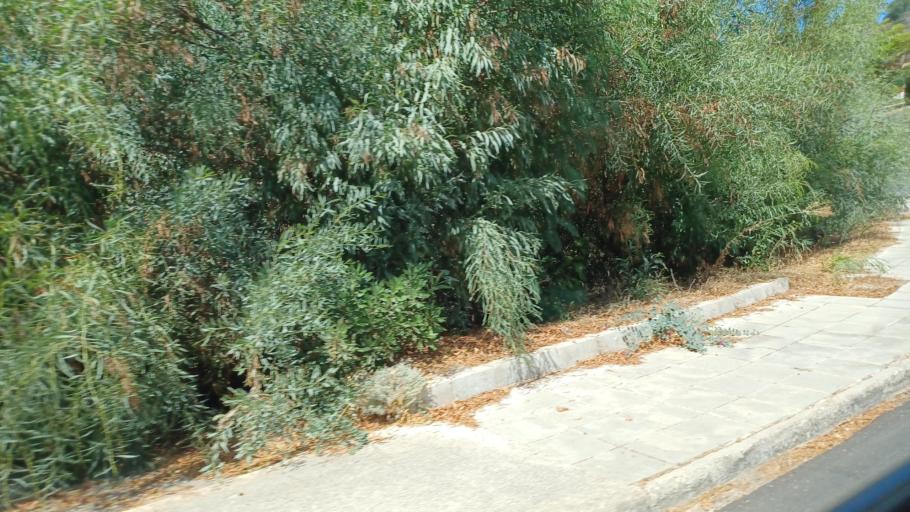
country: CY
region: Pafos
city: Tala
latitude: 34.8441
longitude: 32.4352
